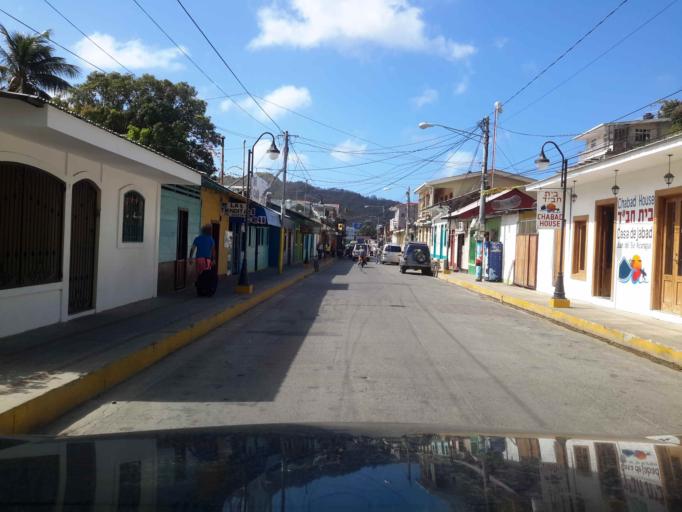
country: NI
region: Rivas
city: San Juan del Sur
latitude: 11.2555
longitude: -85.8703
